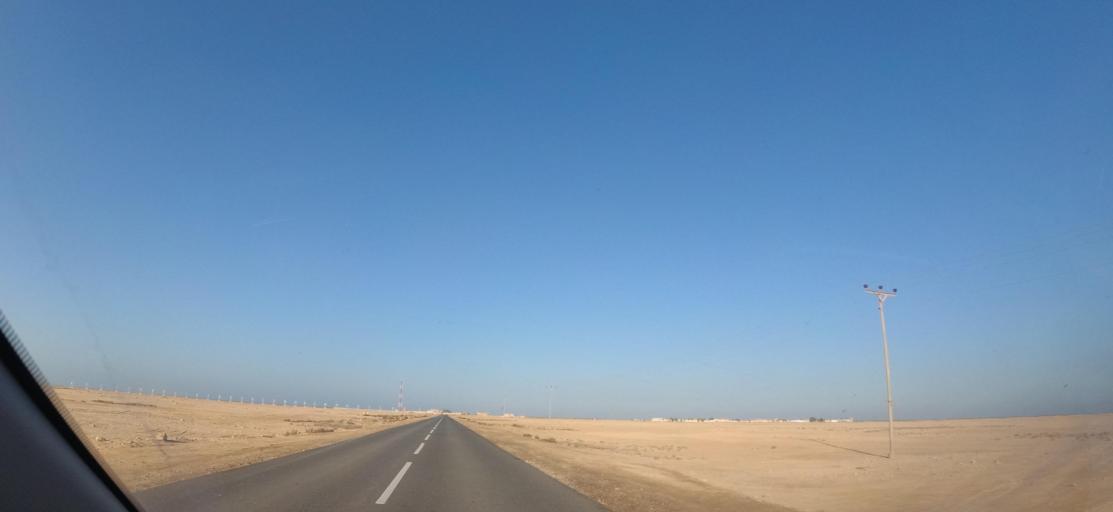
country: QA
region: Madinat ash Shamal
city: Ar Ru'ays
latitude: 26.1478
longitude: 51.2479
